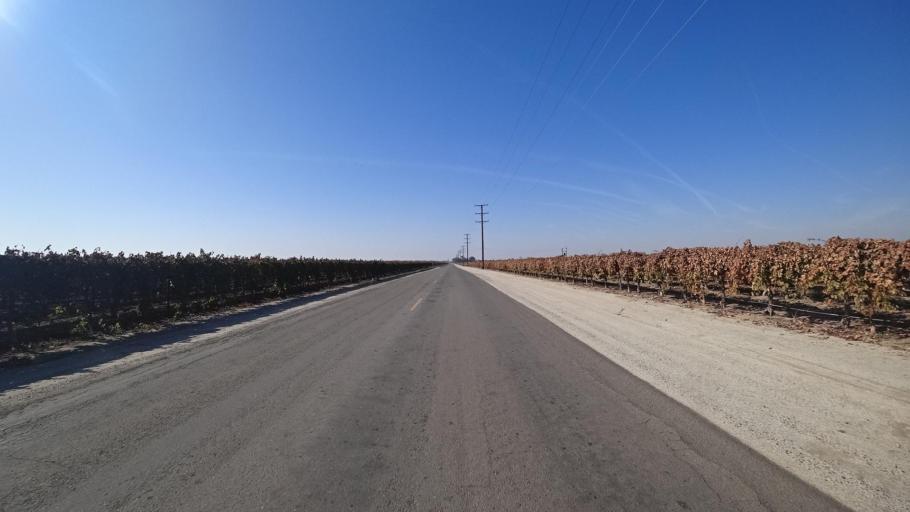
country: US
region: California
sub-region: Kern County
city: McFarland
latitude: 35.7034
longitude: -119.2119
